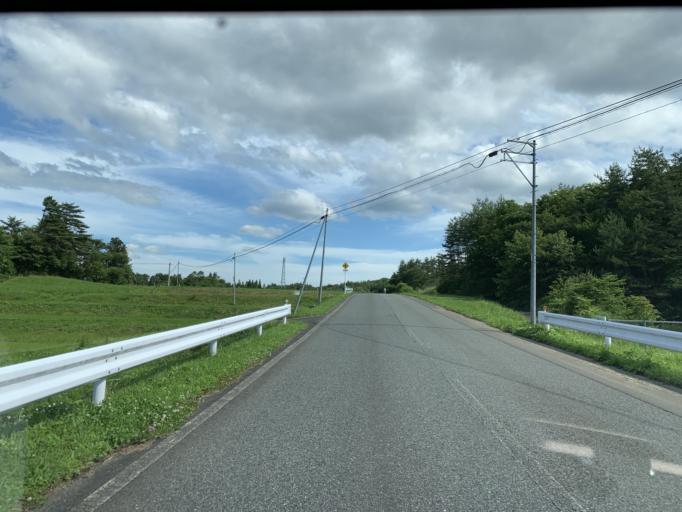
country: JP
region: Iwate
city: Ichinoseki
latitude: 38.9258
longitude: 140.9996
